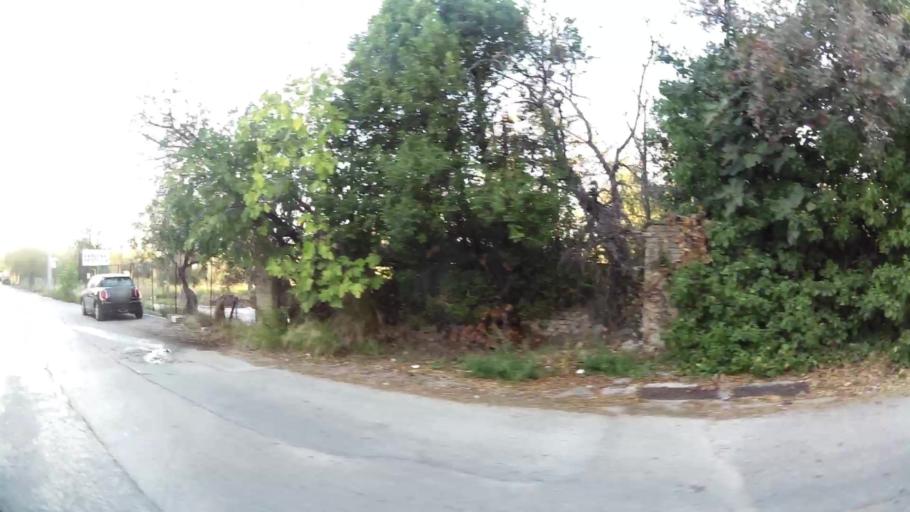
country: GR
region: Attica
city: Pefki
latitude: 38.0687
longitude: 23.7964
